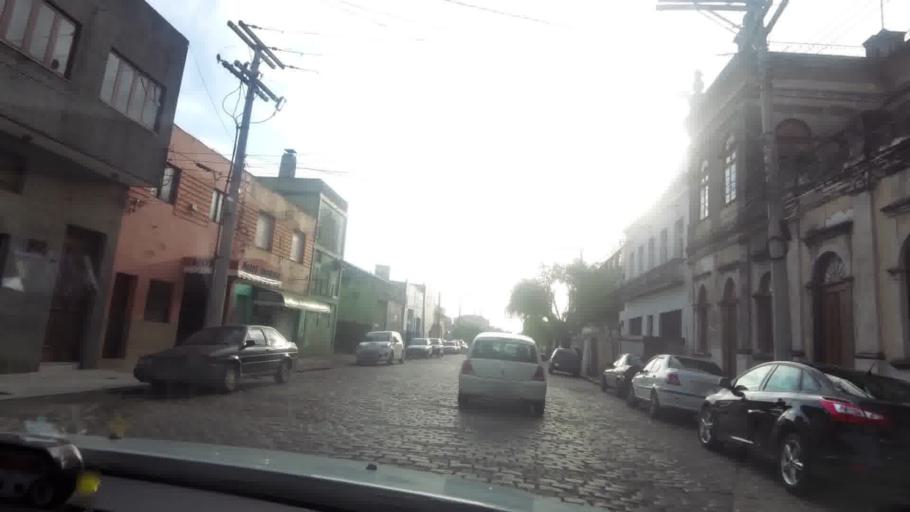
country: BR
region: Rio Grande do Sul
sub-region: Rio Grande
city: Rio Grande
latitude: -32.0318
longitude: -52.0891
